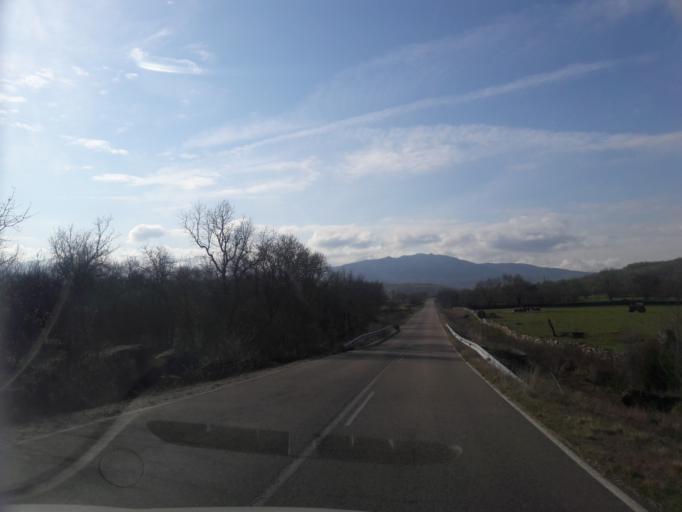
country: ES
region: Castille and Leon
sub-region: Provincia de Salamanca
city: Valdehijaderos
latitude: 40.4265
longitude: -5.8219
